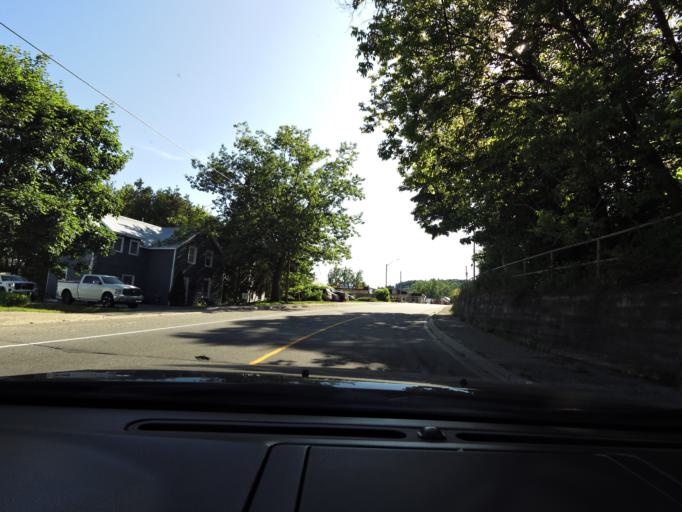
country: CA
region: Ontario
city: Huntsville
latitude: 45.3206
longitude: -79.2350
